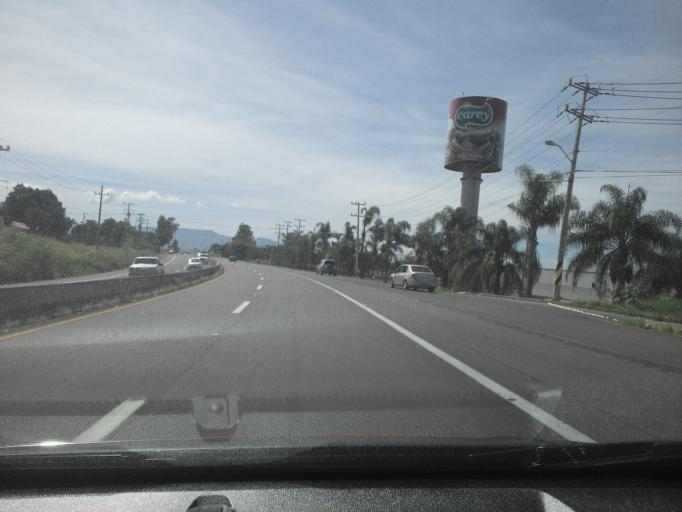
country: MX
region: Jalisco
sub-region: Tala
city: Los Ruisenores
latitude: 20.7029
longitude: -103.6879
